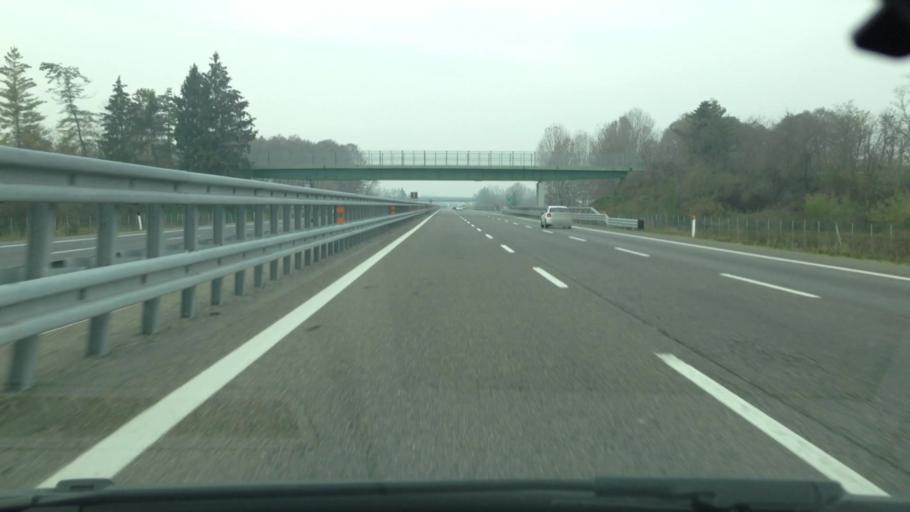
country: IT
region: Piedmont
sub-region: Provincia di Torino
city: Pessione
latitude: 44.9568
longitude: 7.8481
